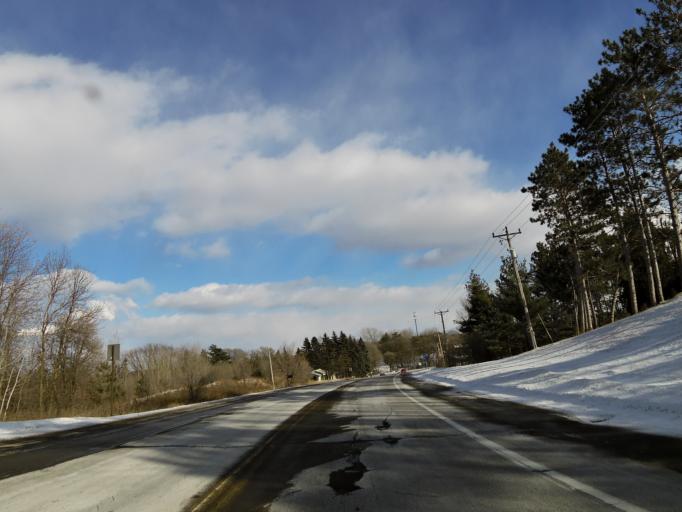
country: US
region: Minnesota
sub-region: Washington County
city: Oak Park Heights
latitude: 45.0179
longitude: -92.8010
